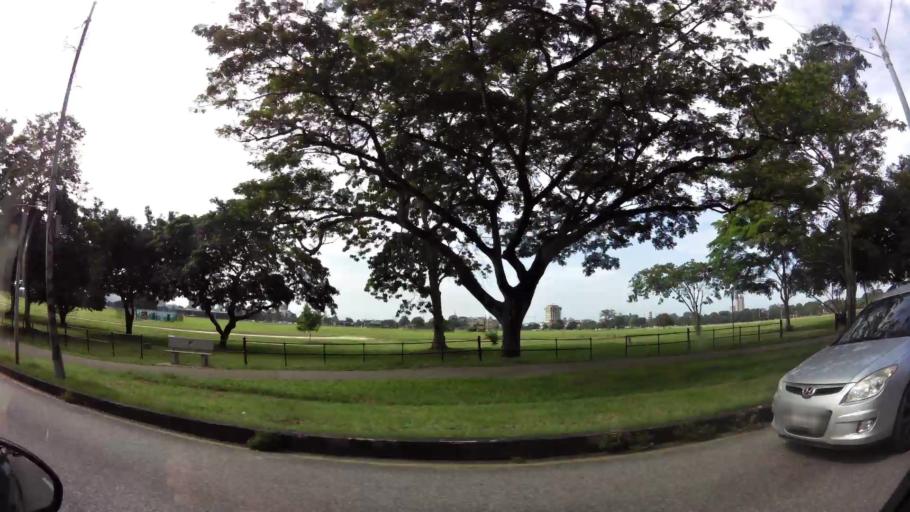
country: TT
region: City of Port of Spain
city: Port-of-Spain
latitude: 10.6722
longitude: -61.5120
